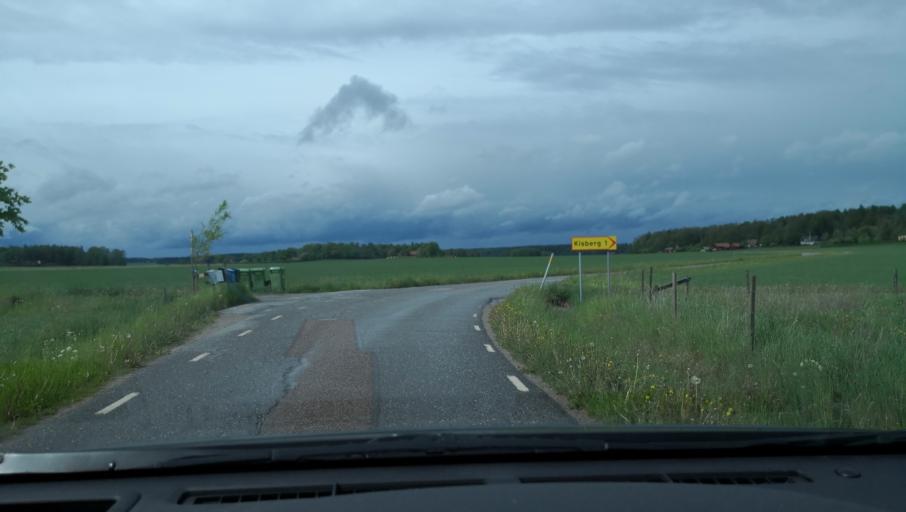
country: SE
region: Uppsala
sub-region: Enkopings Kommun
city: Orsundsbro
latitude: 59.7152
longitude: 17.4239
